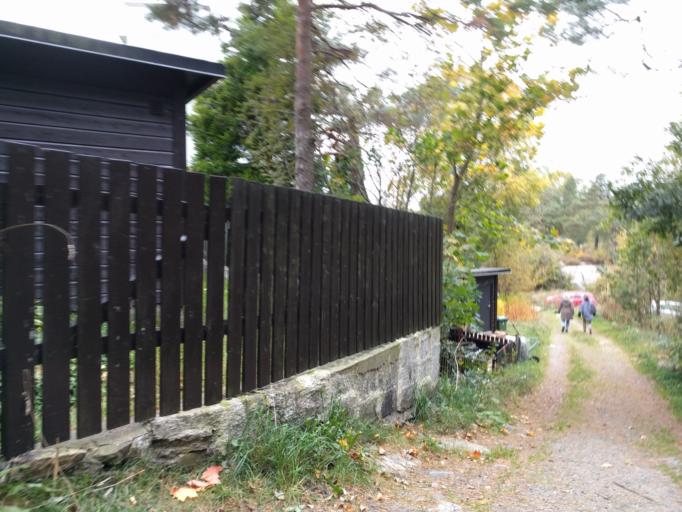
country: NO
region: Vest-Agder
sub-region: Kristiansand
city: Kristiansand
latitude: 58.1445
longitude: 7.9727
